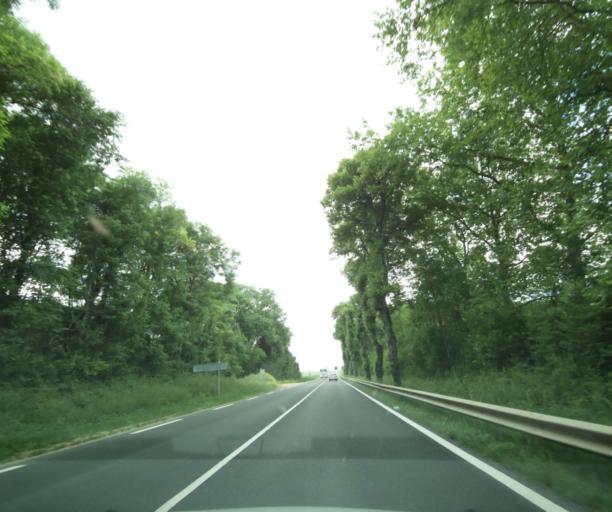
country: FR
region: Centre
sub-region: Departement d'Eure-et-Loir
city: Nogent-le-Phaye
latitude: 48.4043
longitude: 1.5494
